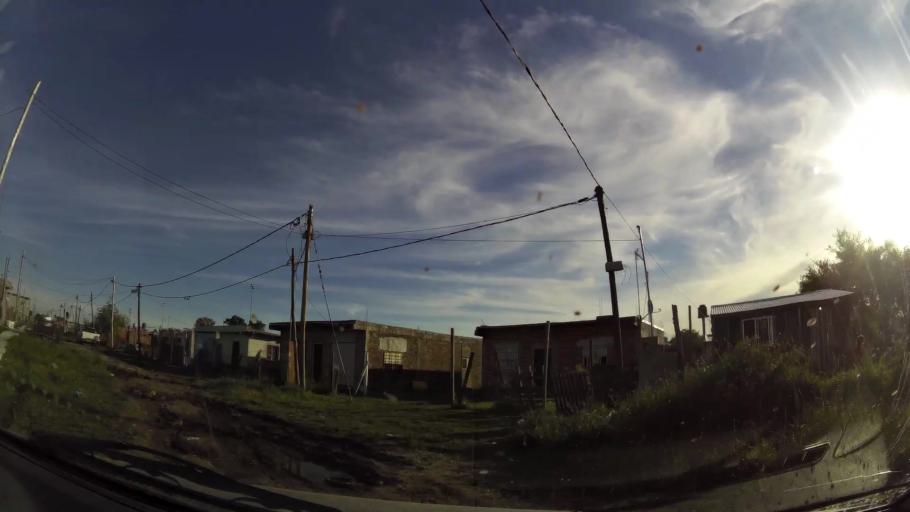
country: AR
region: Buenos Aires
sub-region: Partido de Almirante Brown
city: Adrogue
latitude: -34.8184
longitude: -58.3269
